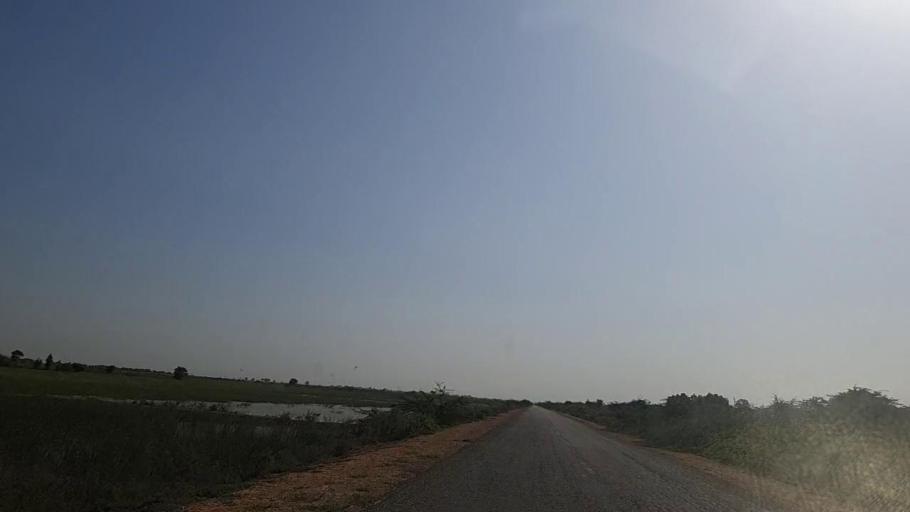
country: PK
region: Sindh
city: Jati
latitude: 24.4489
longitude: 68.2631
